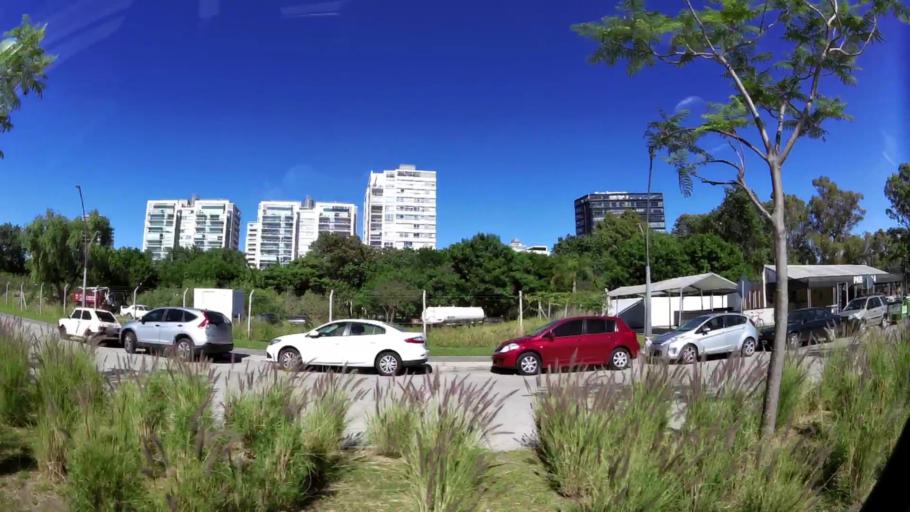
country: AR
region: Buenos Aires
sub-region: Partido de Vicente Lopez
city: Olivos
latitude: -34.5159
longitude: -58.4725
